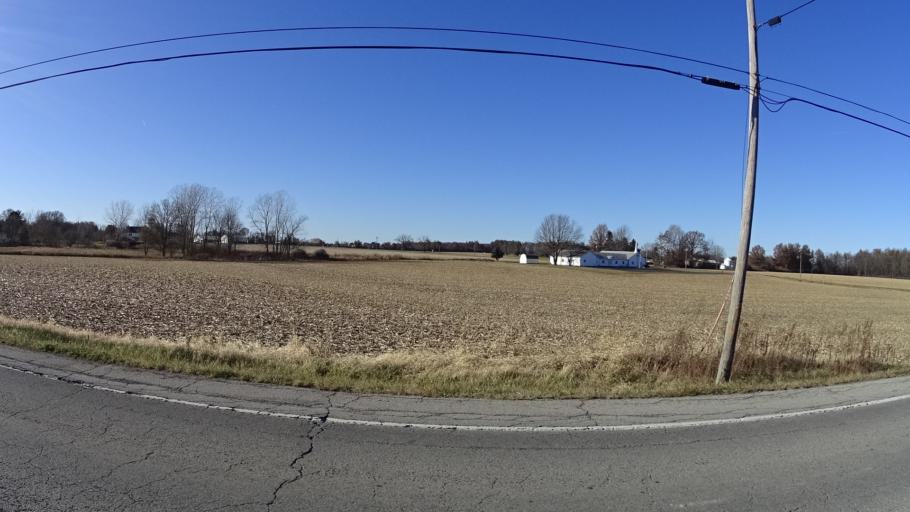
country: US
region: Ohio
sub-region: Lorain County
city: Elyria
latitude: 41.3113
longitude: -82.1447
